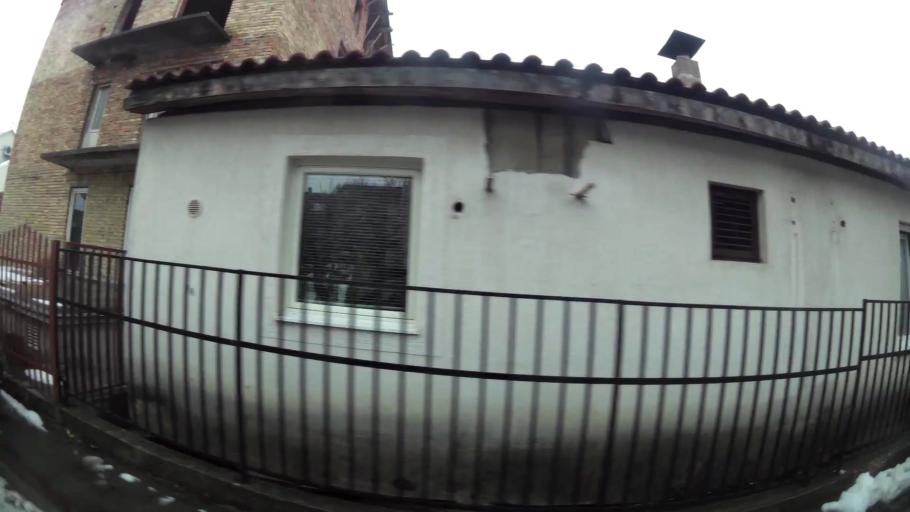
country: RS
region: Central Serbia
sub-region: Belgrade
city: Zvezdara
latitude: 44.7697
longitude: 20.5058
